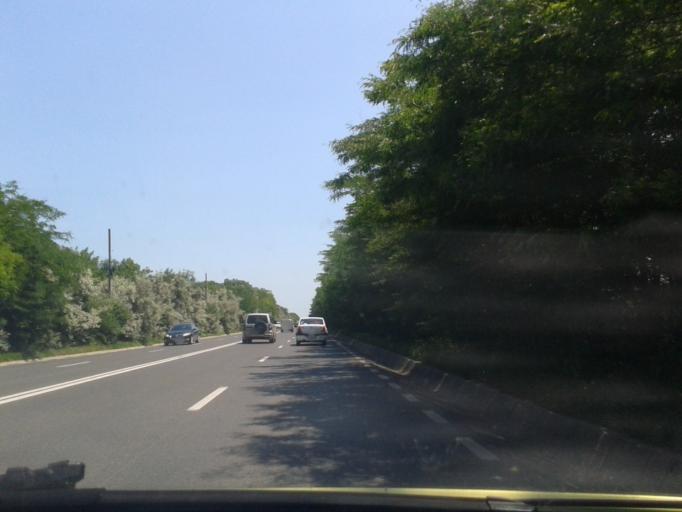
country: RO
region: Constanta
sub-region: Comuna Agigea
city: Agigea
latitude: 44.0856
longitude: 28.6143
